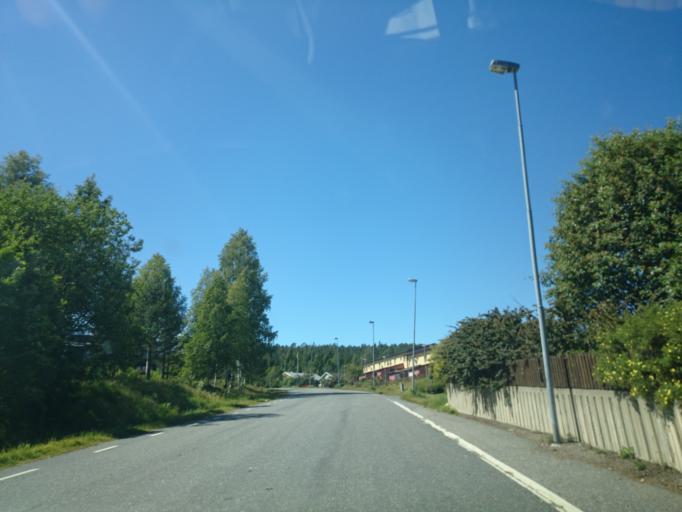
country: SE
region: Vaesternorrland
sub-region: Haernoesands Kommun
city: Haernoesand
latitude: 62.6245
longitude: 17.9106
